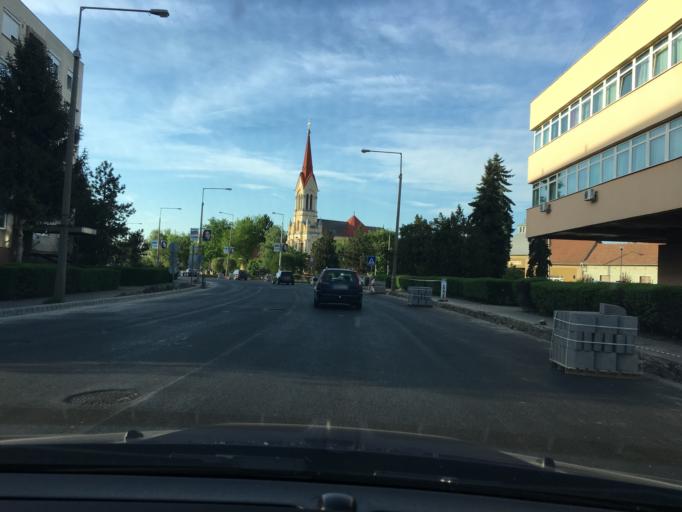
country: HU
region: Hajdu-Bihar
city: Berettyoujfalu
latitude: 47.2254
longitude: 21.5352
